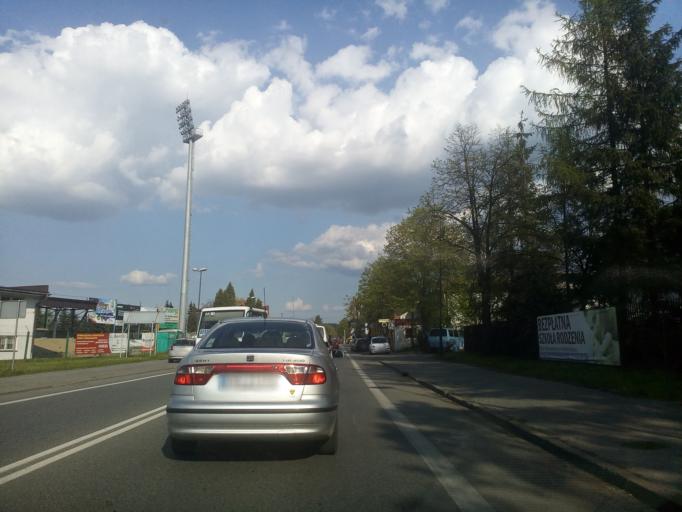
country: PL
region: Lesser Poland Voivodeship
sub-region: Powiat nowosadecki
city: Nowy Sacz
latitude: 49.6201
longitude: 20.7034
